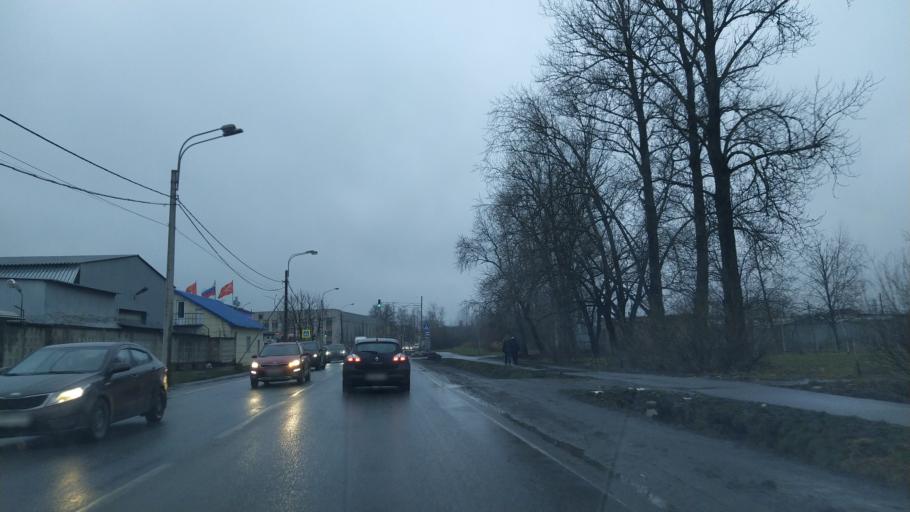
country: RU
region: St.-Petersburg
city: Tyarlevo
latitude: 59.7240
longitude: 30.4425
